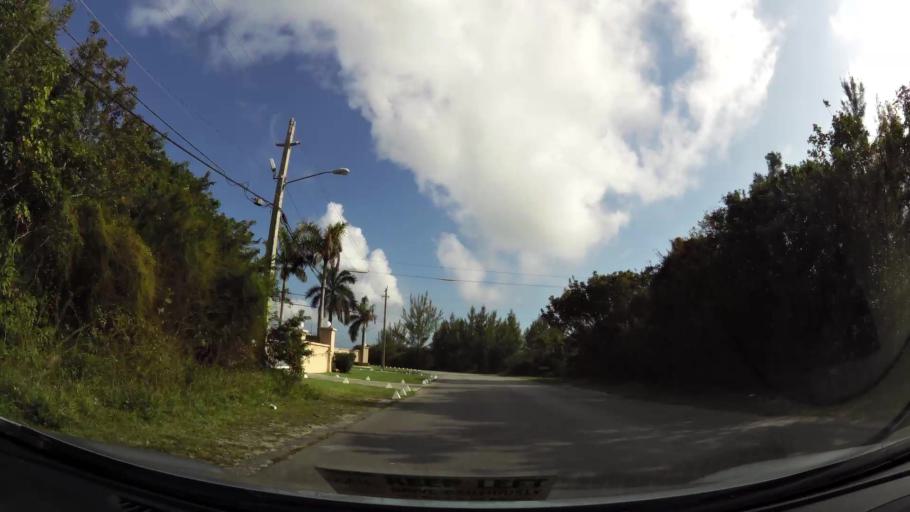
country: BS
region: Freeport
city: Lucaya
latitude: 26.4986
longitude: -78.6697
